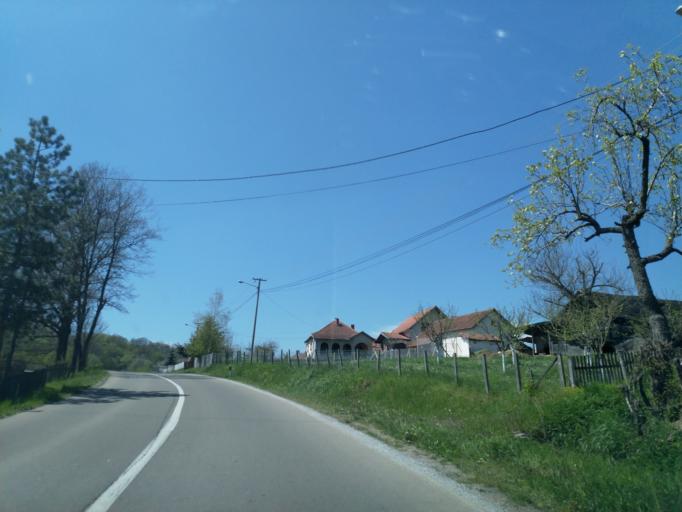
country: RS
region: Central Serbia
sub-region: Belgrade
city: Lazarevac
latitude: 44.3482
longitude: 20.3926
